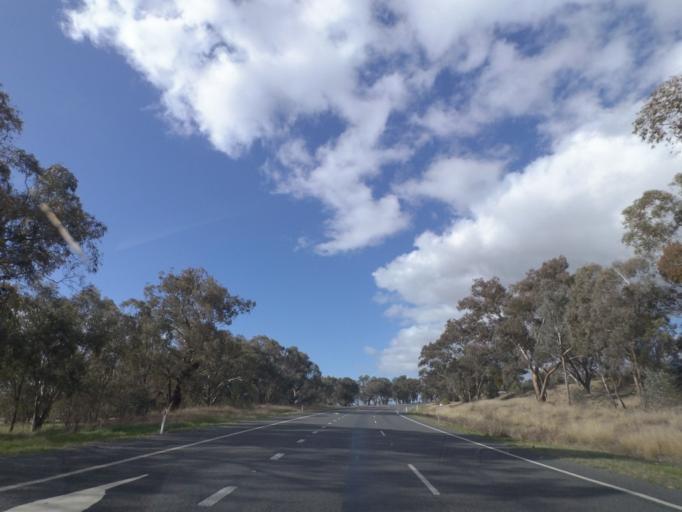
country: AU
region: New South Wales
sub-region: Greater Hume Shire
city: Holbrook
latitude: -35.6742
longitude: 147.3764
